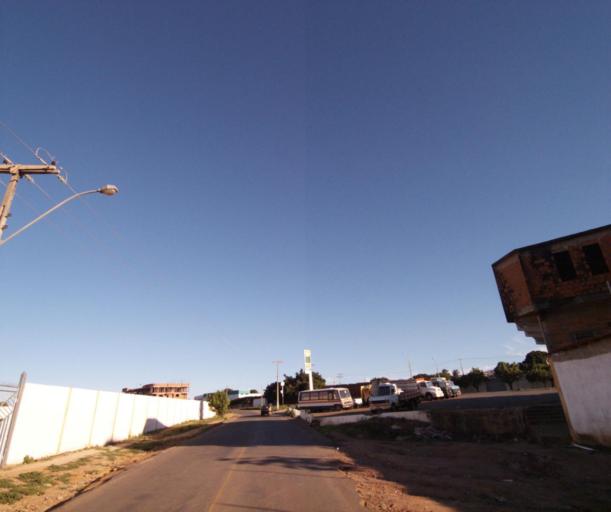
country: BR
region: Bahia
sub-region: Guanambi
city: Guanambi
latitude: -14.2100
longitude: -42.7902
